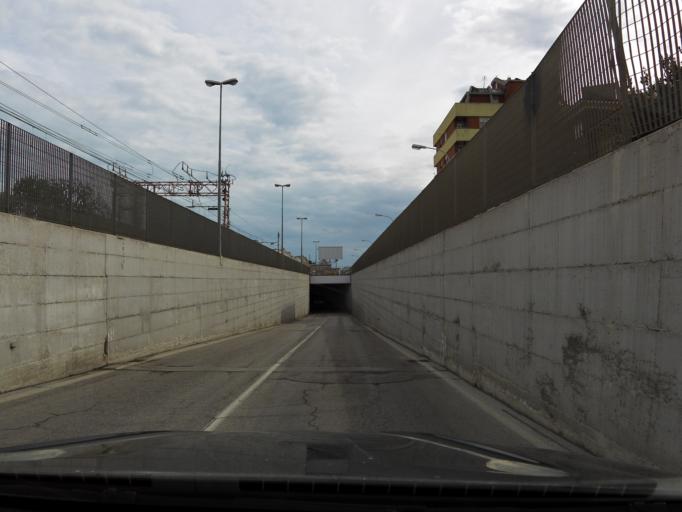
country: IT
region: The Marches
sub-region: Provincia di Macerata
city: Civitanova Marche
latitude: 43.3172
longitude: 13.7217
